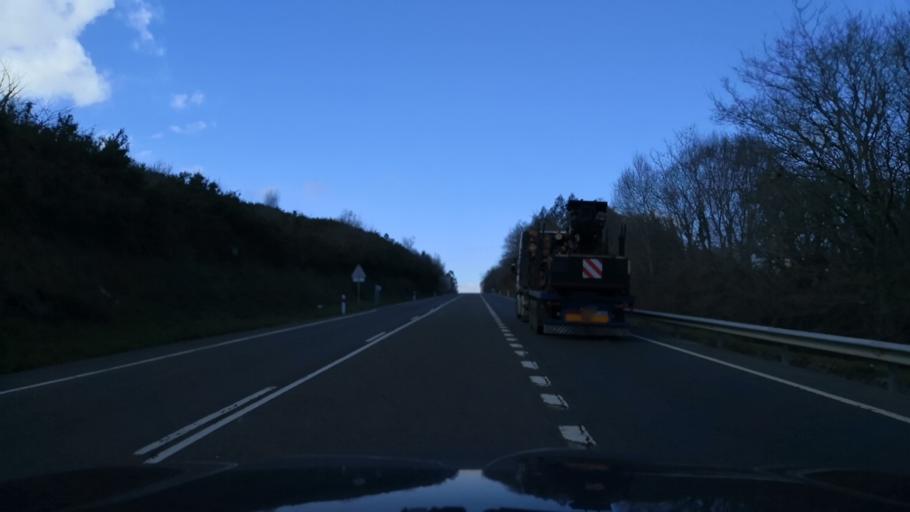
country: ES
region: Galicia
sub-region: Provincia de Pontevedra
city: Silleda
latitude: 42.7015
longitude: -8.3404
